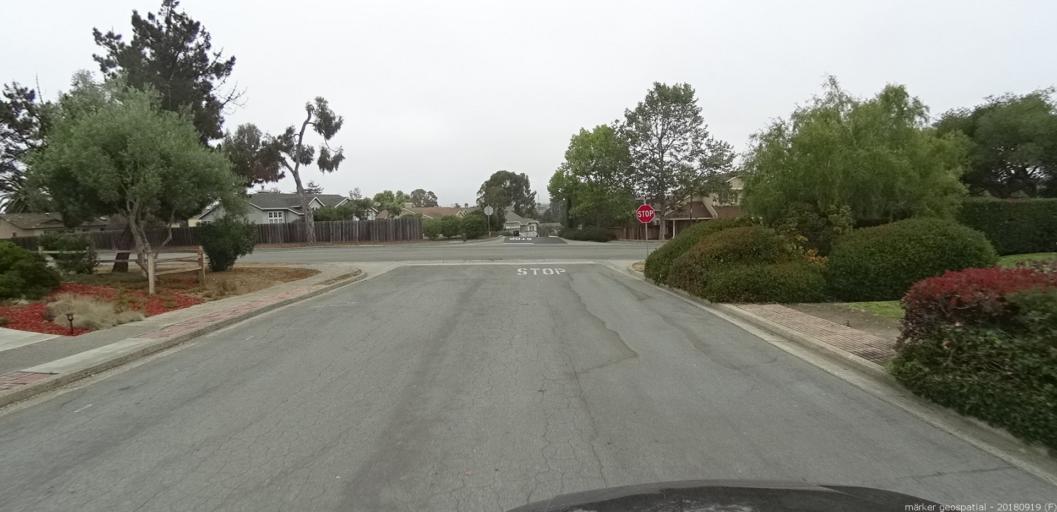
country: US
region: California
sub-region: Monterey County
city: Castroville
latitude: 36.7745
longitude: -121.7273
